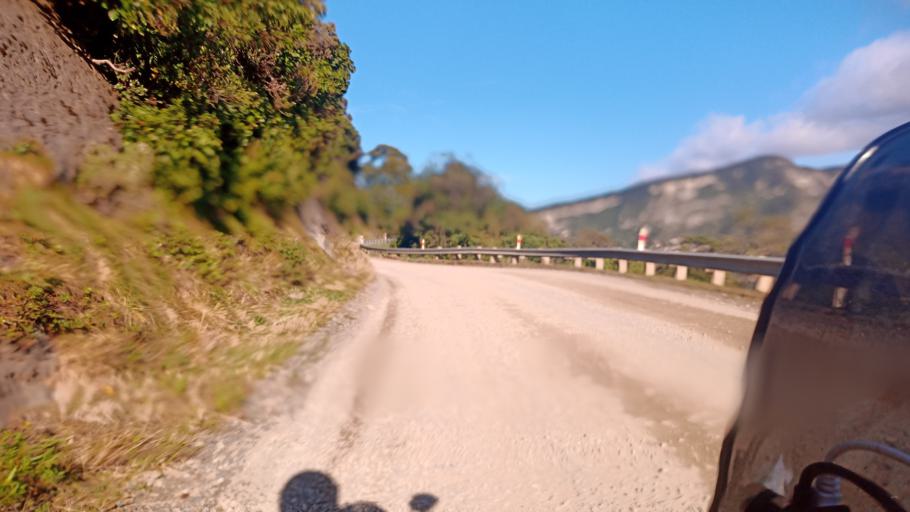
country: NZ
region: Hawke's Bay
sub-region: Wairoa District
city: Wairoa
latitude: -38.7881
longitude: 177.1293
